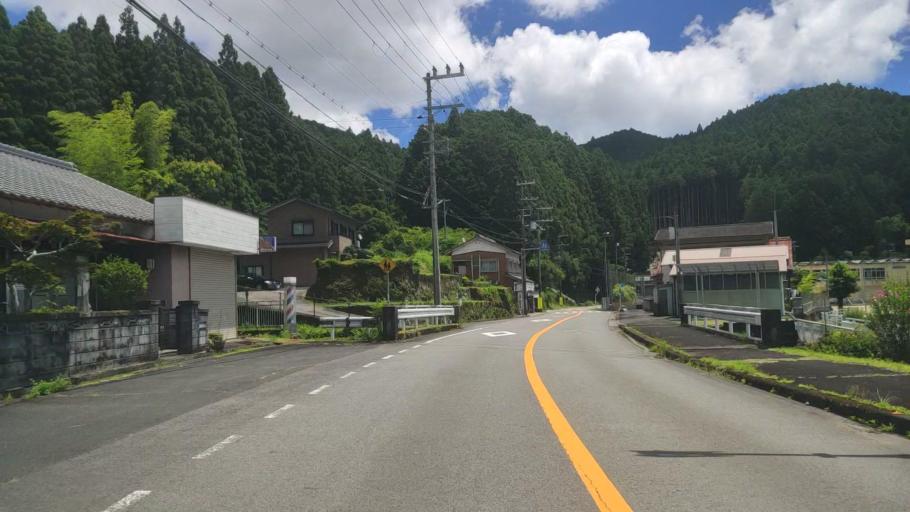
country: JP
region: Mie
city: Owase
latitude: 33.9494
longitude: 136.0755
